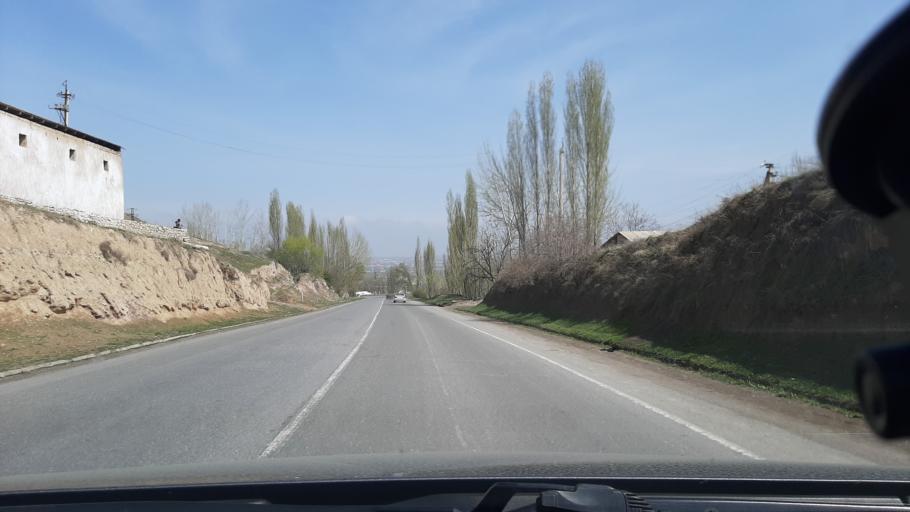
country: TJ
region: Viloyati Sughd
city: Istaravshan
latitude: 39.8662
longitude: 68.9915
